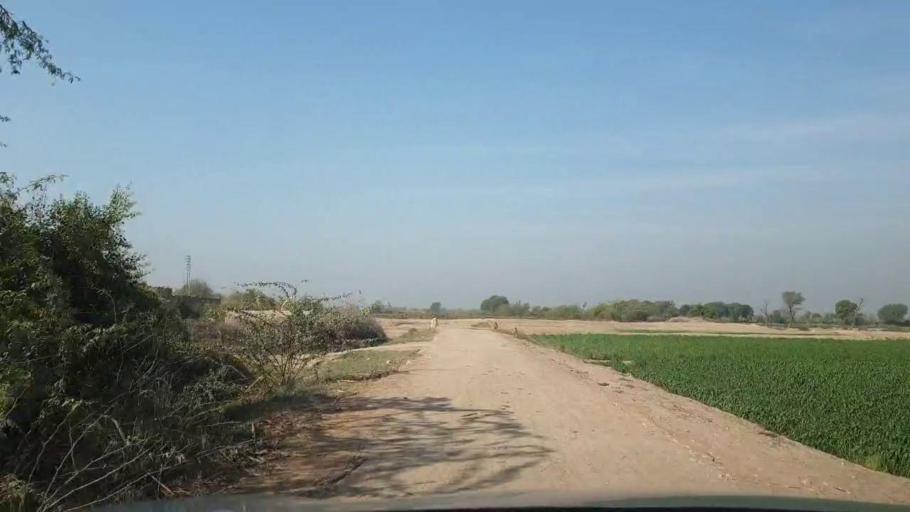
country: PK
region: Sindh
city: Tando Allahyar
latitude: 25.5892
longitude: 68.7352
